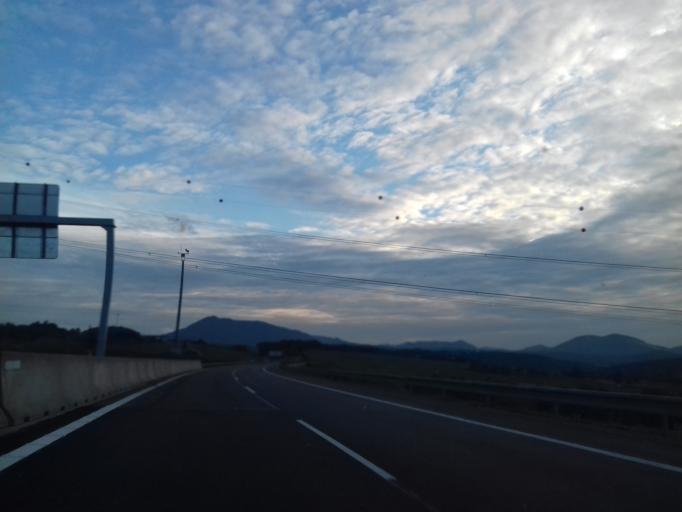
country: SK
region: Trenciansky
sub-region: Okres Povazska Bystrica
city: Povazska Bystrica
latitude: 49.0881
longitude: 18.4192
